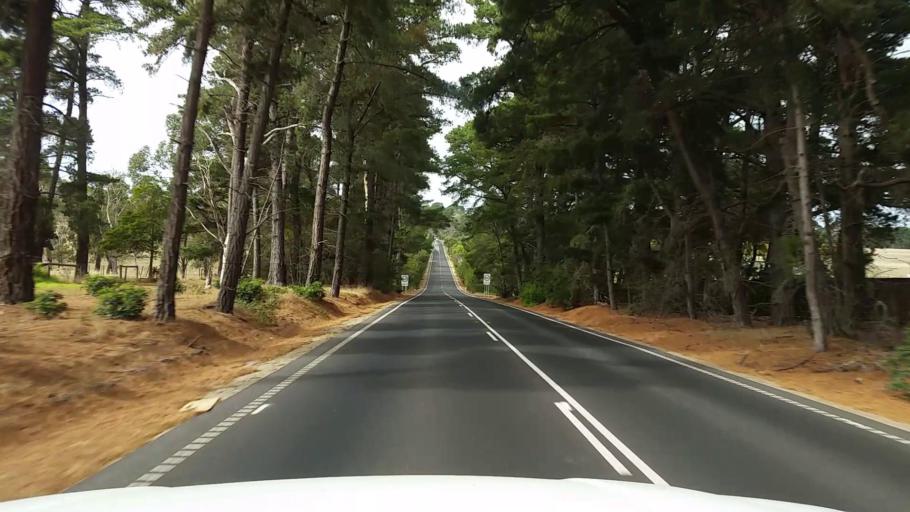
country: AU
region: Victoria
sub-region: Mornington Peninsula
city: Balnarring
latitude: -38.3589
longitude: 145.1123
